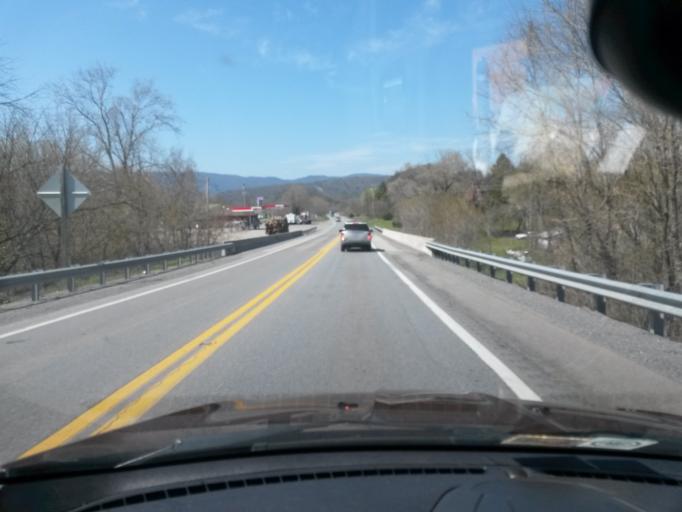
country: US
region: Virginia
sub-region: Alleghany County
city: Clifton Forge
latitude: 37.6876
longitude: -79.8094
